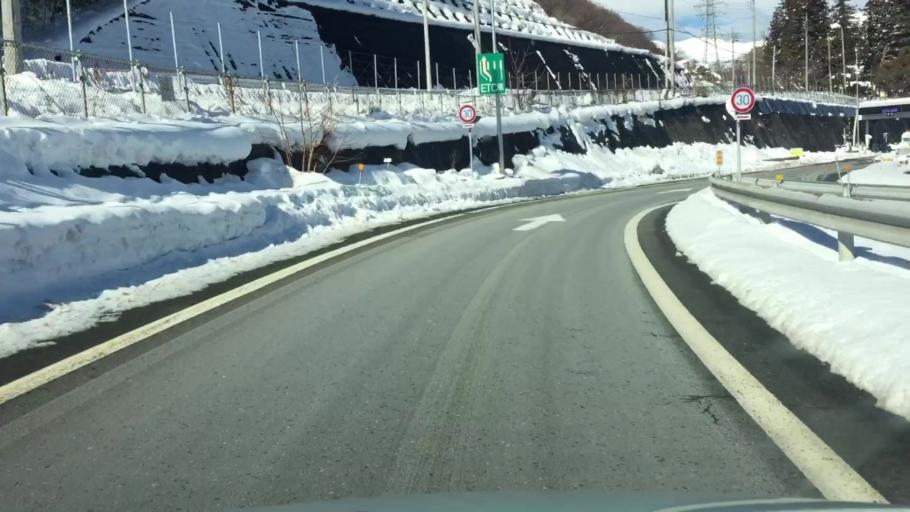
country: JP
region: Gunma
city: Numata
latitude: 36.7466
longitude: 138.9741
